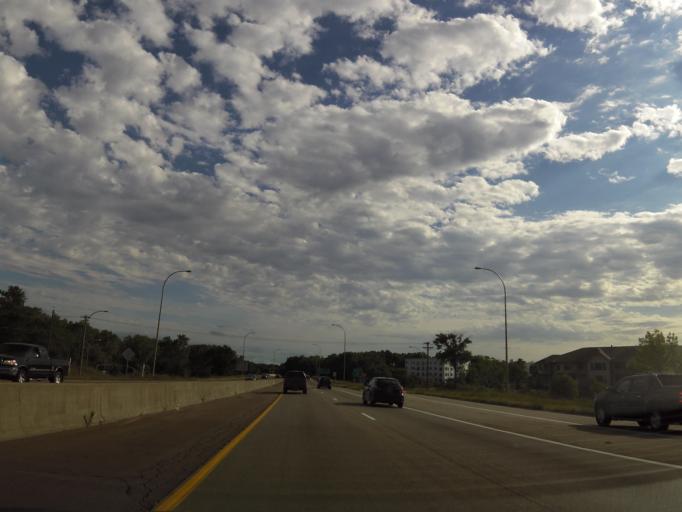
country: US
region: Minnesota
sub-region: Hennepin County
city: Minnetonka Mills
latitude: 44.9485
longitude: -93.4007
